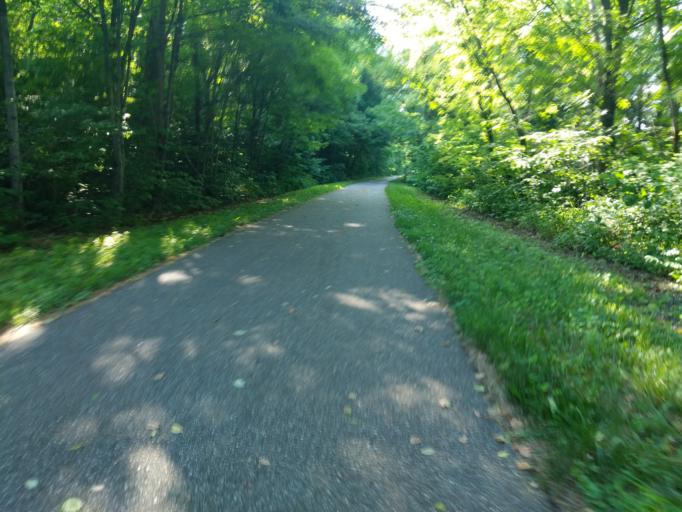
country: US
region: Ohio
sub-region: Athens County
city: Nelsonville
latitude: 39.4284
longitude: -82.2026
